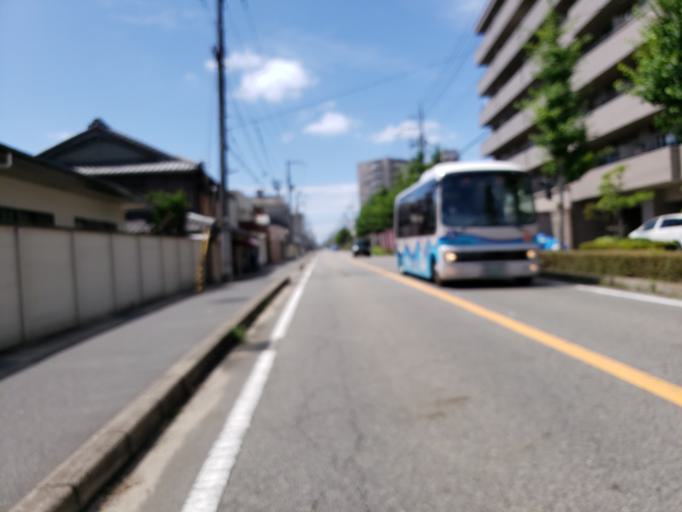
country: JP
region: Hyogo
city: Kakogawacho-honmachi
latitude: 34.7140
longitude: 134.8900
